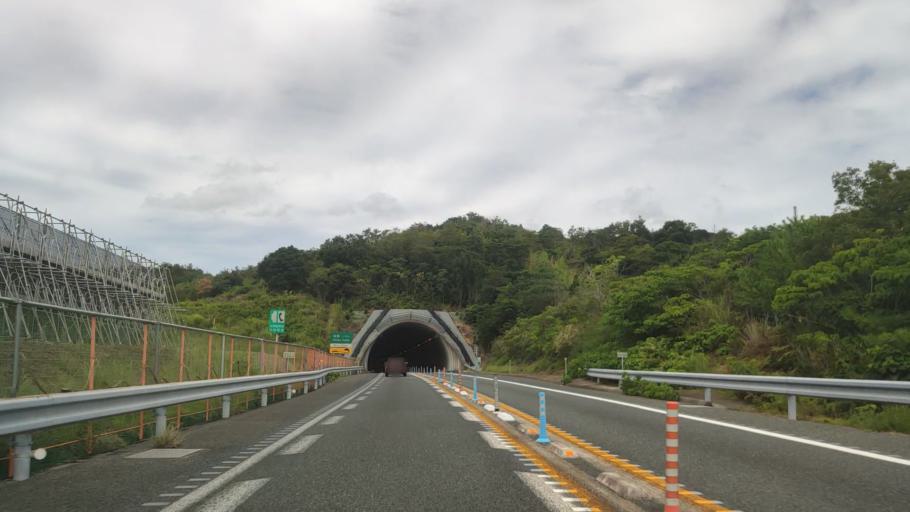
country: JP
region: Wakayama
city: Gobo
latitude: 33.8753
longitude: 135.1874
